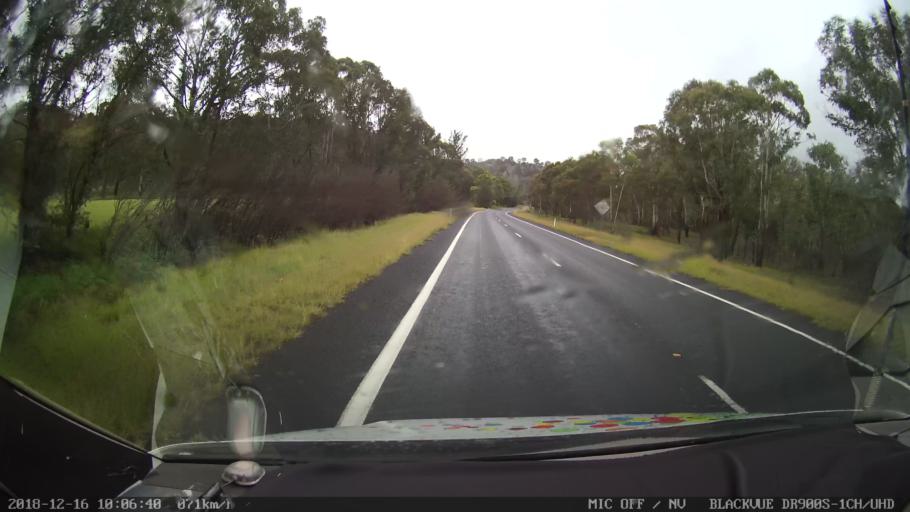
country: AU
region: New South Wales
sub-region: Glen Innes Severn
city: Glen Innes
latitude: -29.3429
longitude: 151.8923
